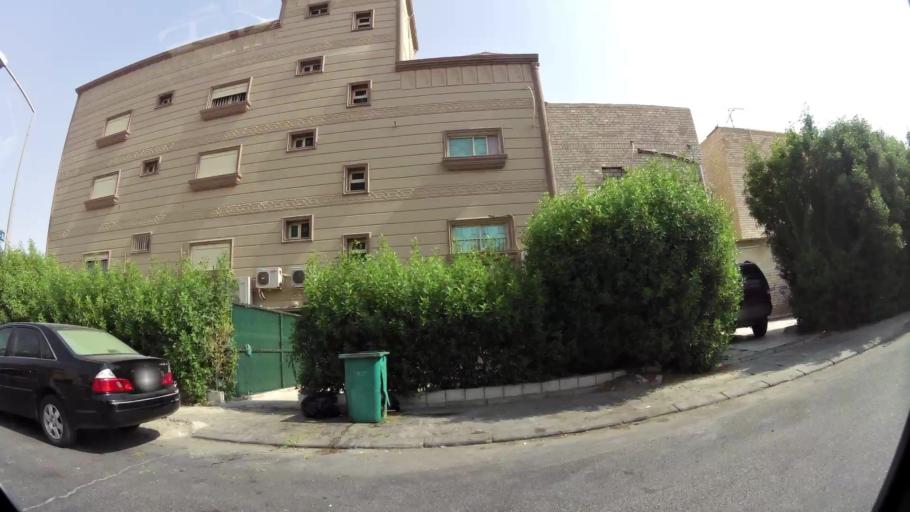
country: KW
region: Muhafazat al Jahra'
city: Al Jahra'
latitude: 29.3265
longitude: 47.6588
